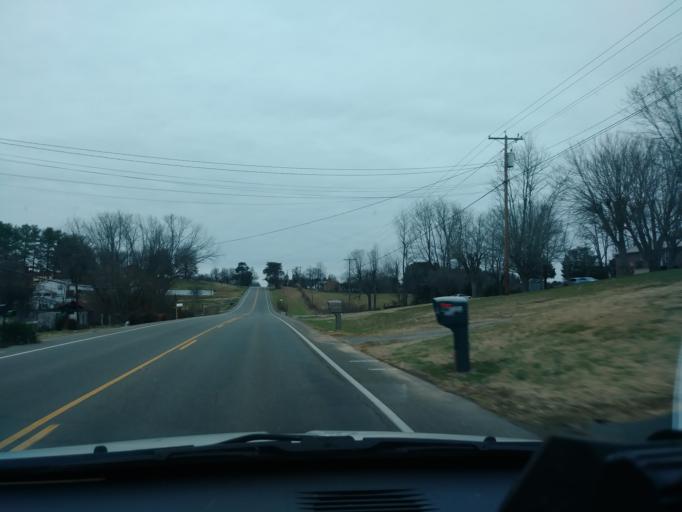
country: US
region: Tennessee
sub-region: Greene County
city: Greeneville
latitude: 36.0928
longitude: -82.8708
